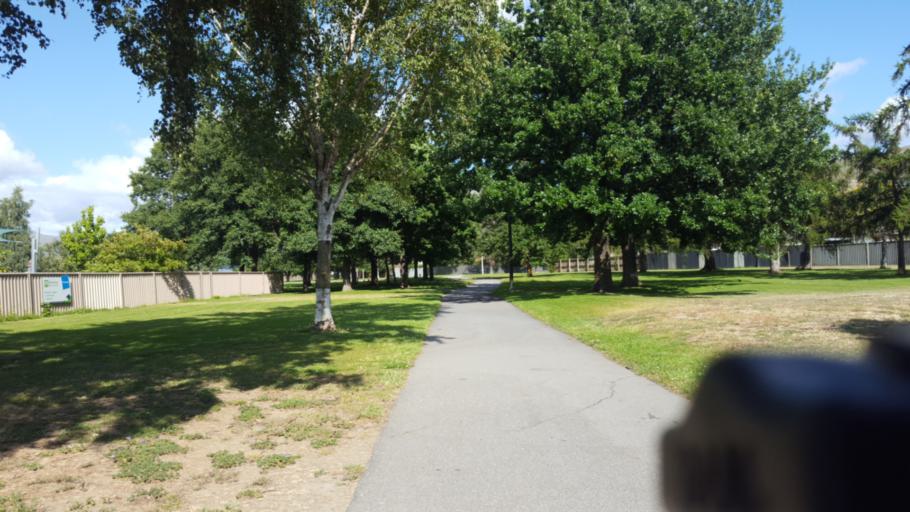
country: NZ
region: Otago
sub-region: Queenstown-Lakes District
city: Wanaka
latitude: -45.0424
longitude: 169.1862
